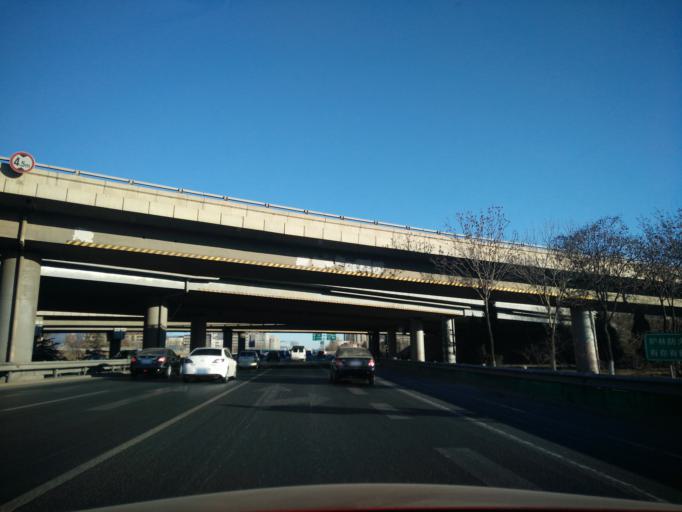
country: CN
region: Beijing
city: Lugu
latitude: 39.8926
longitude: 116.2053
